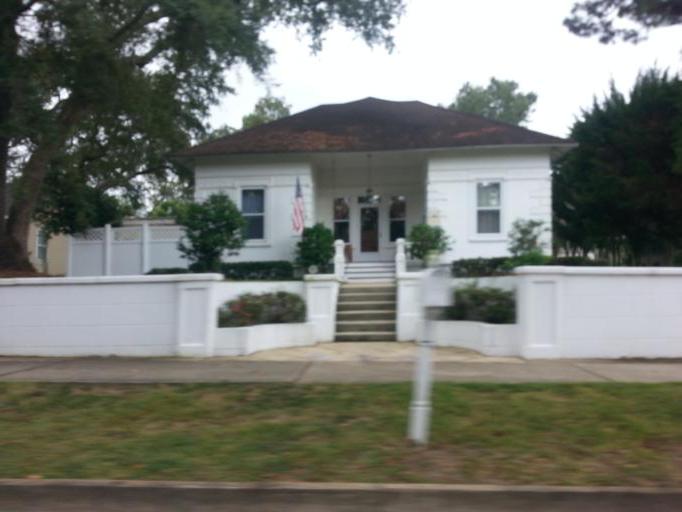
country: US
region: Alabama
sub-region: Baldwin County
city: Fairhope
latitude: 30.5190
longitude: -87.9062
